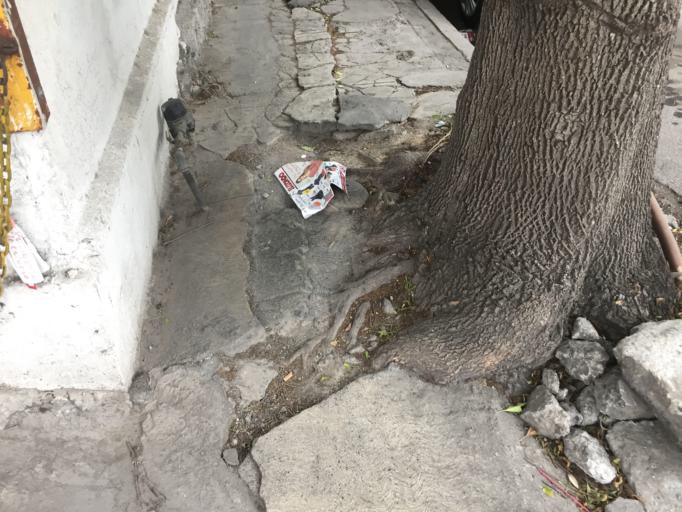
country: MX
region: Nuevo Leon
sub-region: Monterrey
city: Monterrey
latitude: 25.6790
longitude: -100.3042
